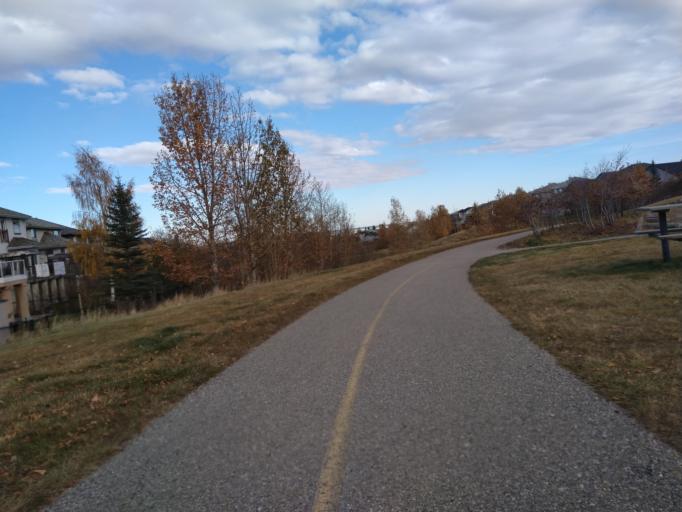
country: CA
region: Alberta
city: Calgary
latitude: 51.1390
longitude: -114.1292
